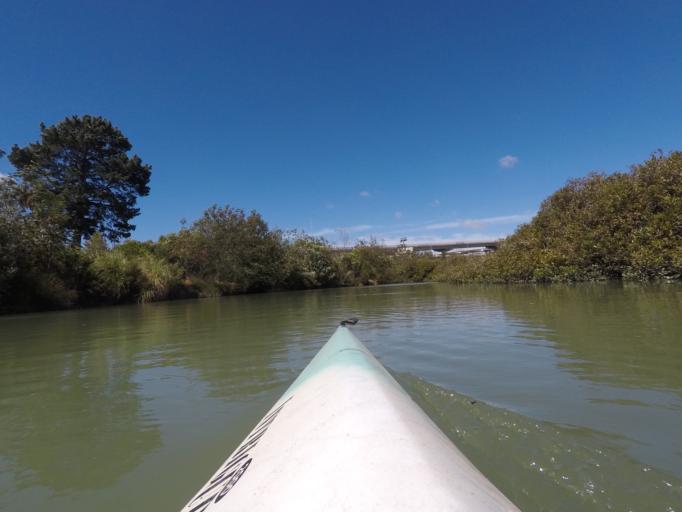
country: NZ
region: Auckland
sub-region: Auckland
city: Rosebank
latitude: -36.8729
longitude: 174.6998
